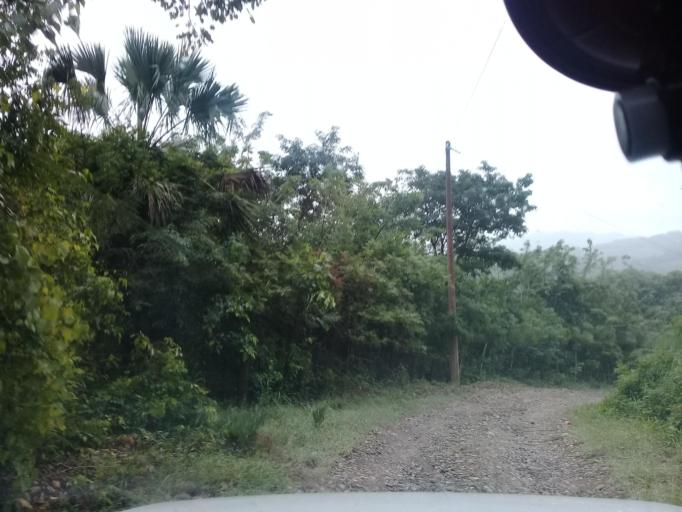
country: MX
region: Veracruz
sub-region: Chalma
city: San Pedro Coyutla
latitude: 21.2451
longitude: -98.4179
